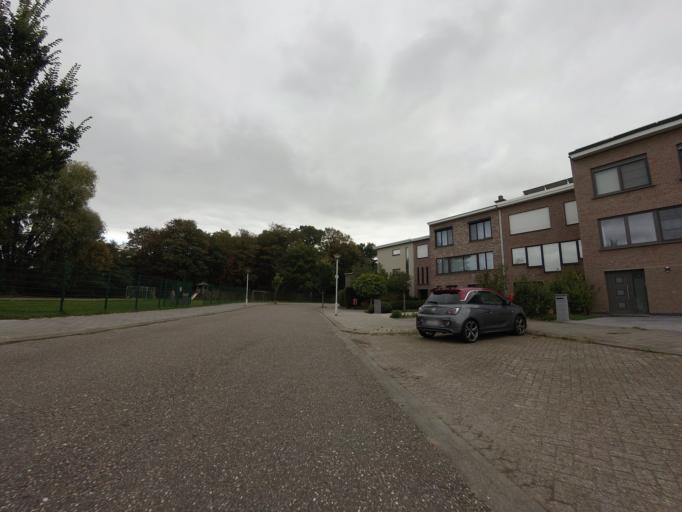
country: BE
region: Flanders
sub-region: Provincie Antwerpen
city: Antwerpen
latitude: 51.2460
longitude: 4.4331
